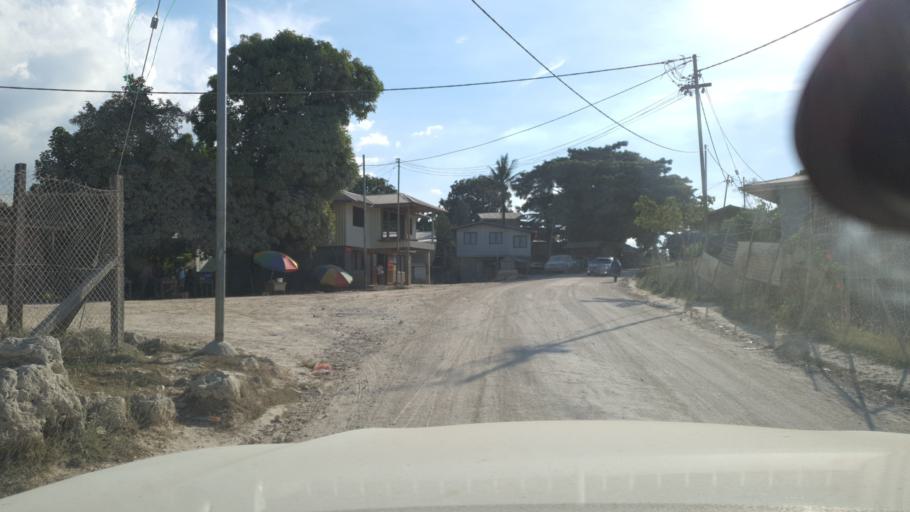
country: SB
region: Guadalcanal
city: Honiara
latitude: -9.4532
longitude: 159.9908
